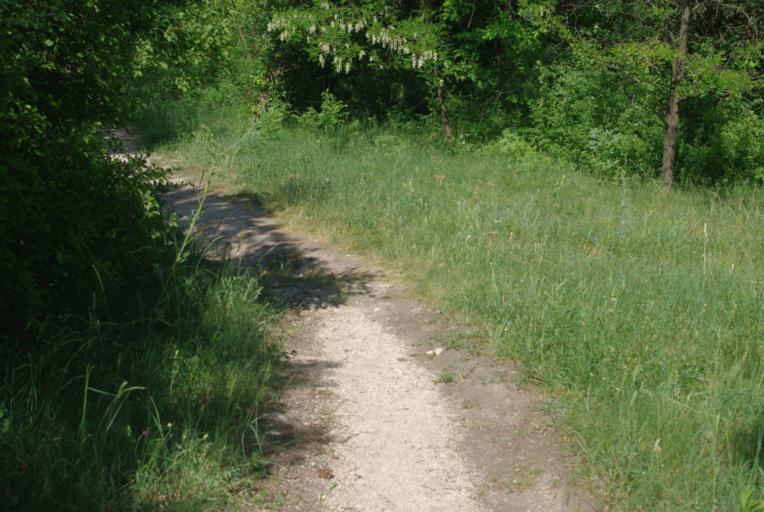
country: HU
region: Pest
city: Pilisszentivan
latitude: 47.6046
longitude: 18.8772
